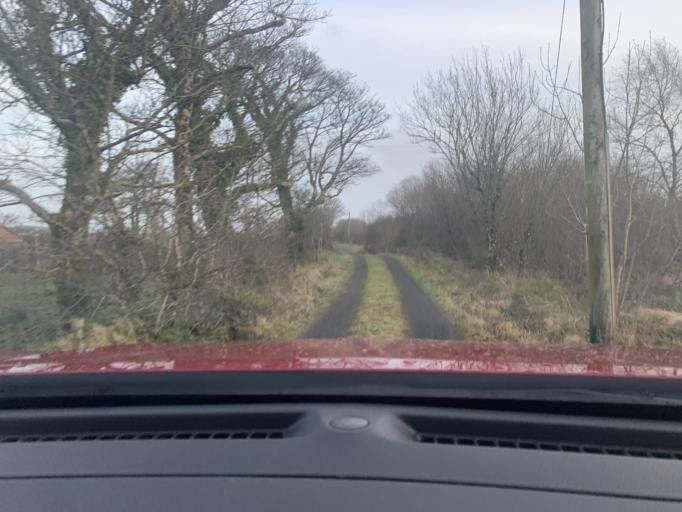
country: IE
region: Connaught
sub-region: Roscommon
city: Ballaghaderreen
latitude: 53.9531
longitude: -8.5382
